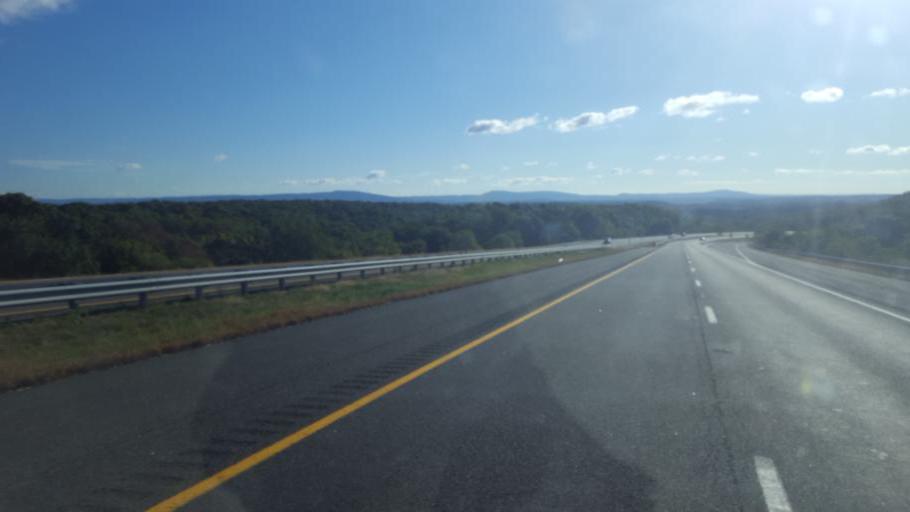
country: US
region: Maryland
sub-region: Washington County
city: Hancock
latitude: 39.7090
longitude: -78.2688
